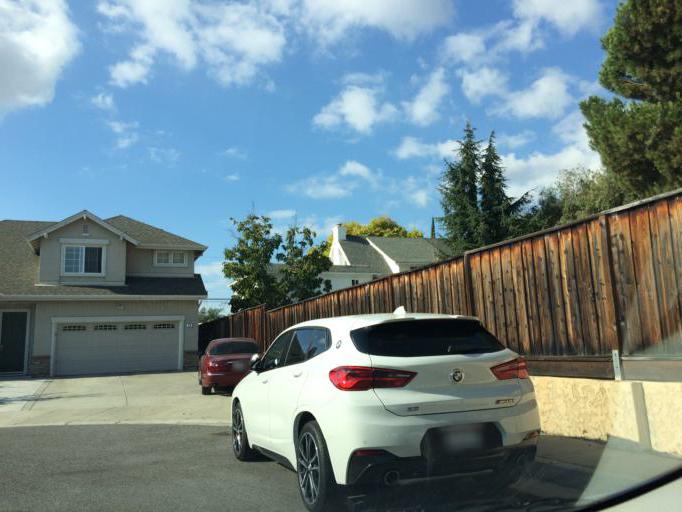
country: US
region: California
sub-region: Santa Clara County
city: East Foothills
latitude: 37.3746
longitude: -121.8208
